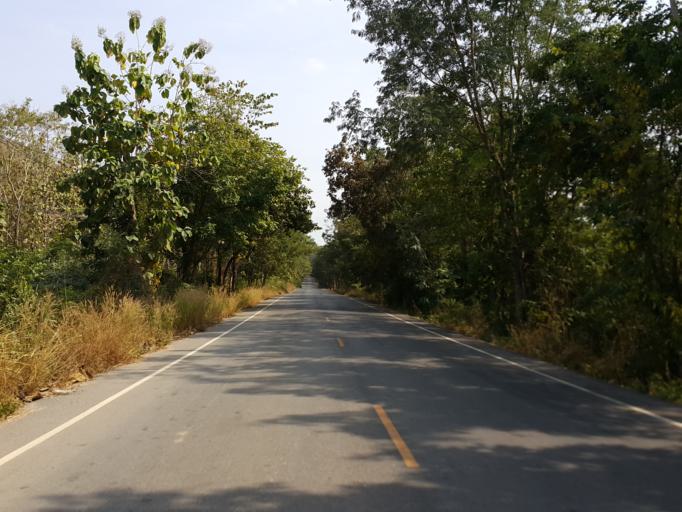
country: TH
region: Sukhothai
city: Thung Saliam
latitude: 17.3441
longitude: 99.4485
